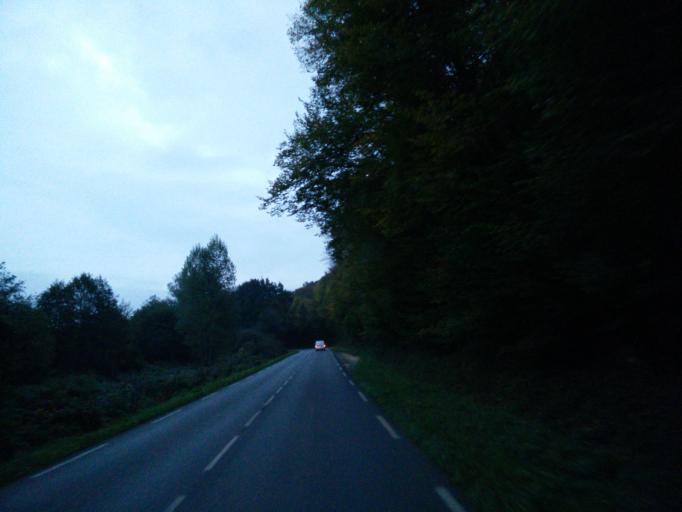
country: FR
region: Aquitaine
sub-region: Departement de la Dordogne
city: Saint-Cyprien
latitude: 44.9456
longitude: 1.0480
